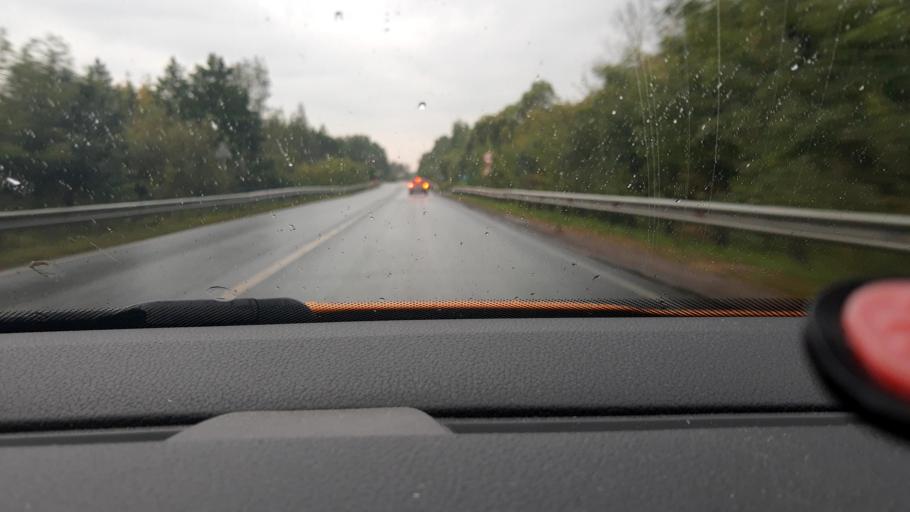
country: RU
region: Moskovskaya
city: Obukhovo
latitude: 55.8119
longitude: 38.2536
